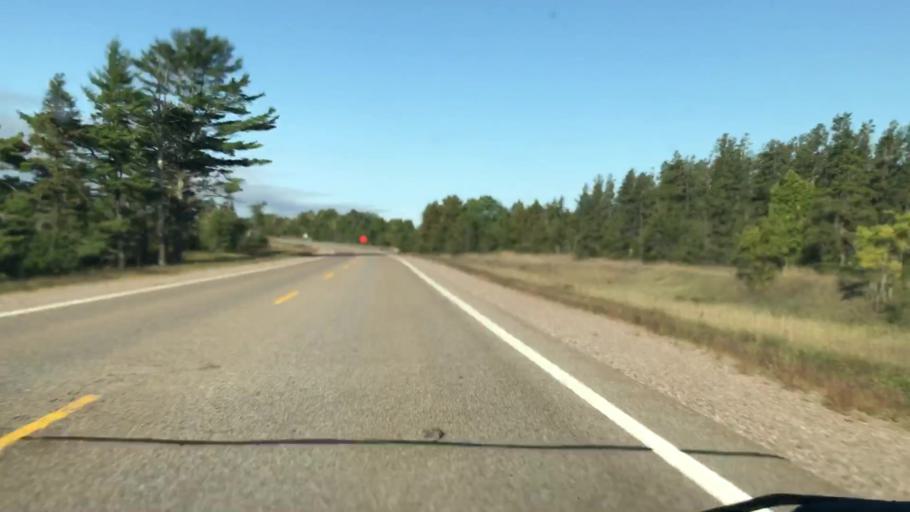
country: US
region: Michigan
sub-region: Mackinac County
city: Saint Ignace
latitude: 46.3583
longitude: -84.8829
